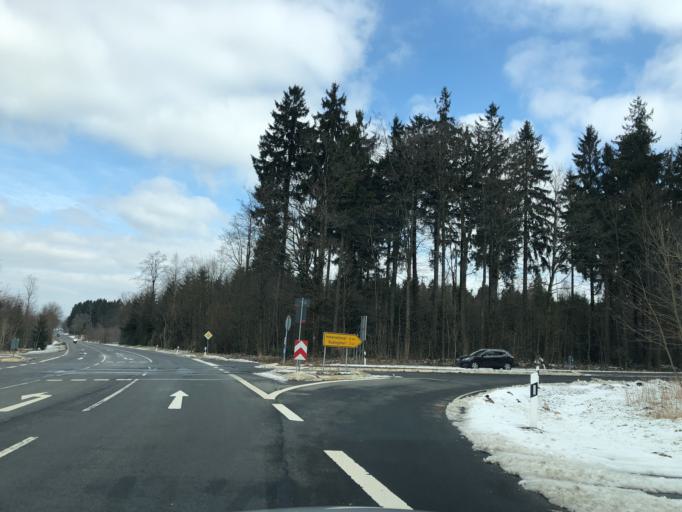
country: DE
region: Hesse
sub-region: Regierungsbezirk Giessen
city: Ulrichstein
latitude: 50.5385
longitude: 9.1979
